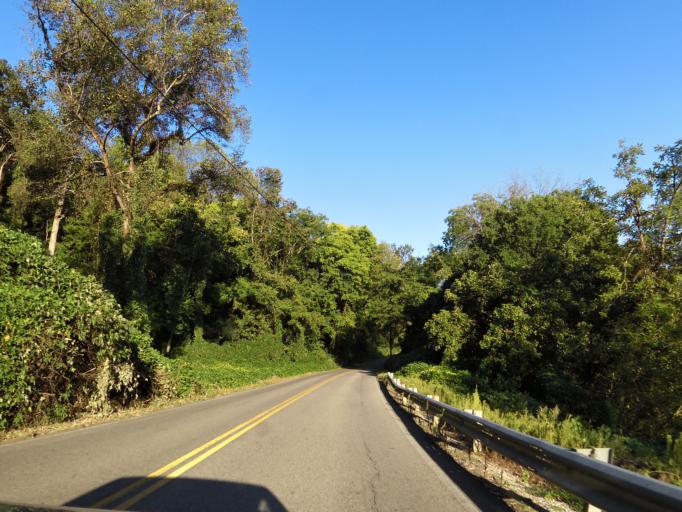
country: US
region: Tennessee
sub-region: Blount County
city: Eagleton Village
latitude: 35.8212
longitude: -83.9319
